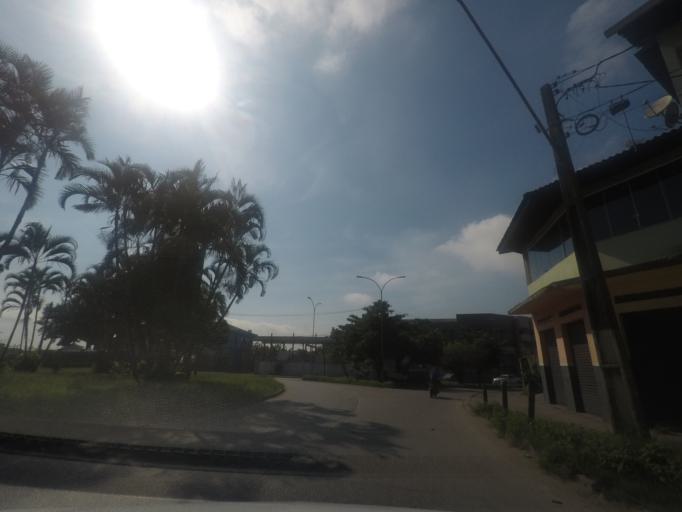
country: BR
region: Parana
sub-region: Paranagua
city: Paranagua
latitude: -25.5152
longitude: -48.5226
